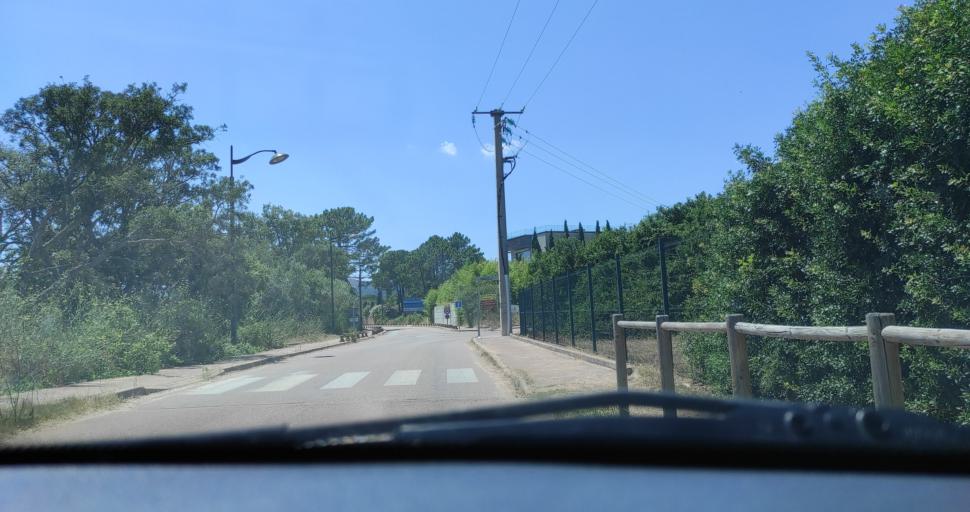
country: FR
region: Corsica
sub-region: Departement de la Corse-du-Sud
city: Porto-Vecchio
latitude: 41.6246
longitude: 9.3365
